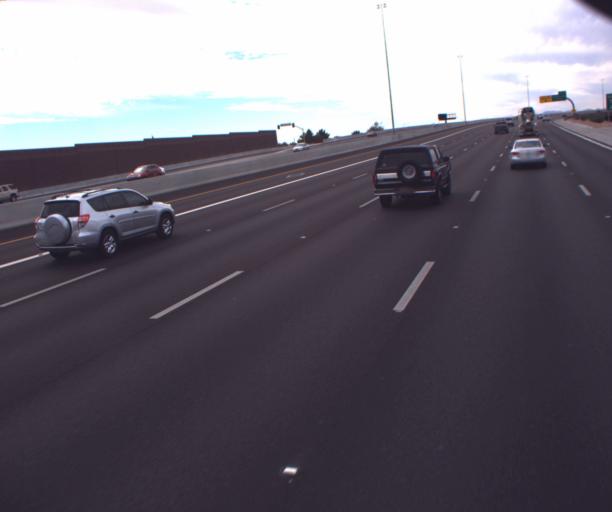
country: US
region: Arizona
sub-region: Maricopa County
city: Mesa
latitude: 33.4476
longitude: -111.8532
